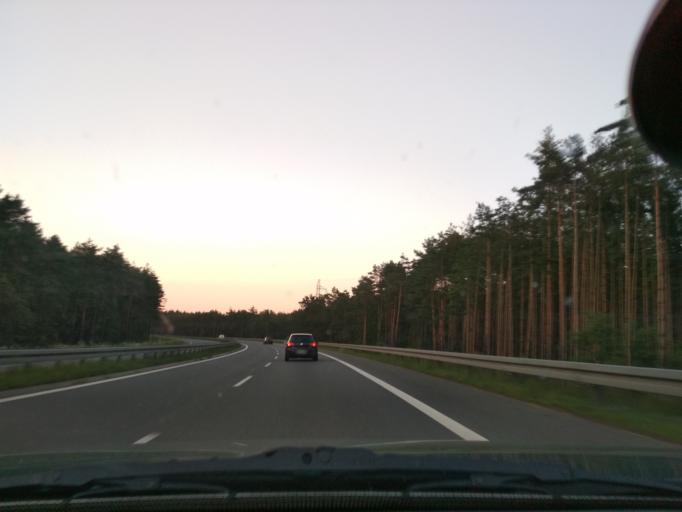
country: PL
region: Silesian Voivodeship
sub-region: Powiat bedzinski
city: Siewierz
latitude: 50.4644
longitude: 19.2495
